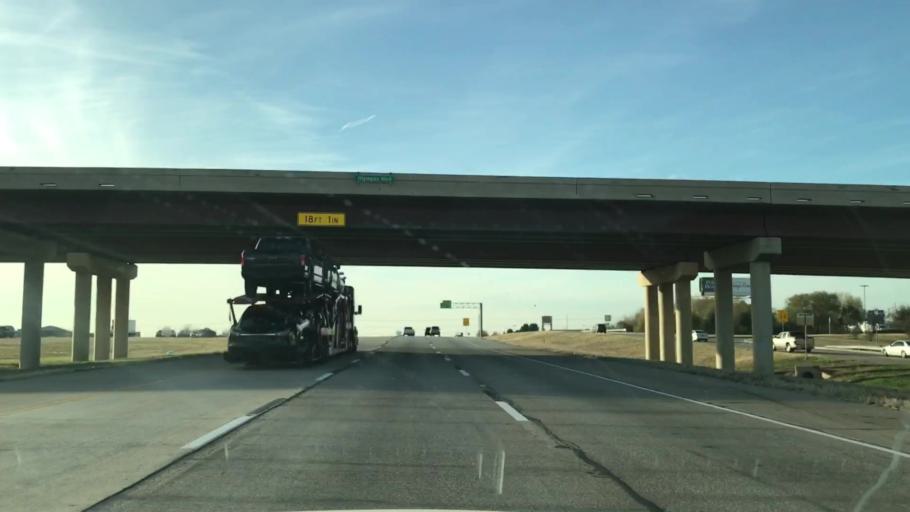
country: US
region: Texas
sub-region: Dallas County
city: Coppell
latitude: 32.9194
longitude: -96.9746
